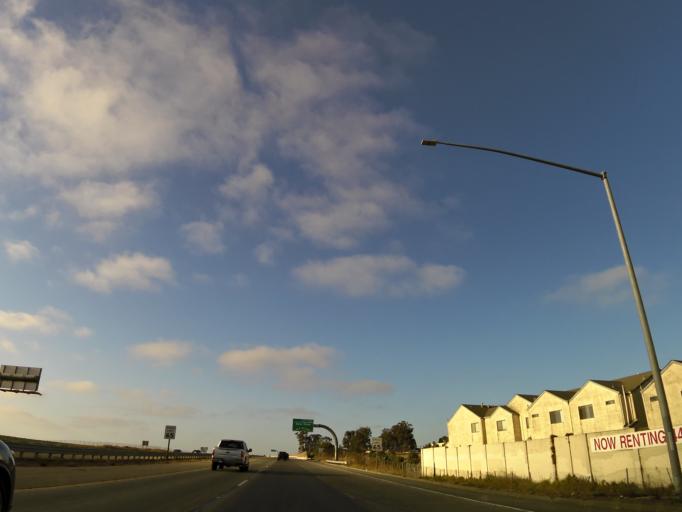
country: US
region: California
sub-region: Monterey County
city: Boronda
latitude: 36.7267
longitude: -121.6584
